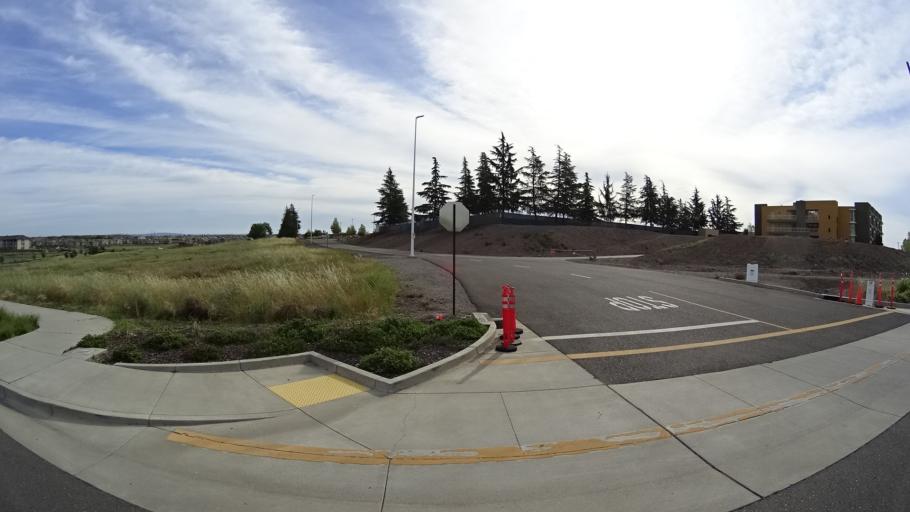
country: US
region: California
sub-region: Placer County
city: Rocklin
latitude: 38.8205
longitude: -121.2956
